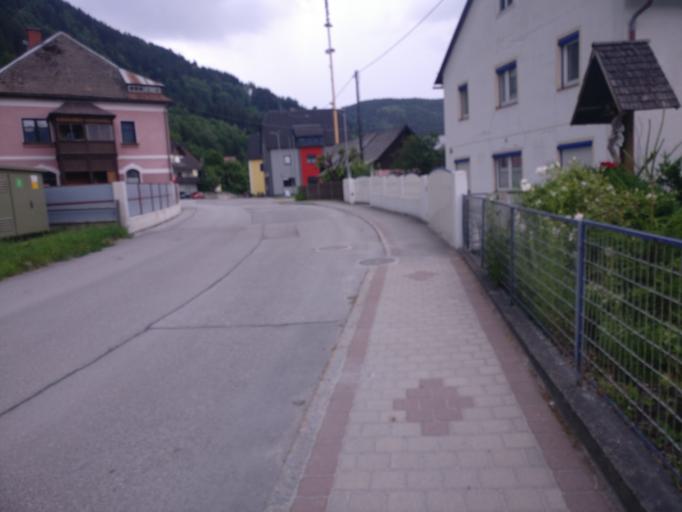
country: AT
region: Styria
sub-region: Politischer Bezirk Liezen
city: Selzthal
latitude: 47.5522
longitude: 14.3204
